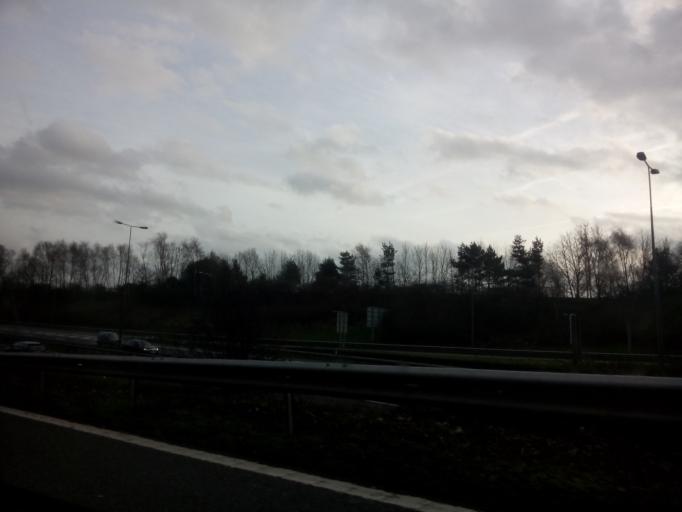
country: GB
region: England
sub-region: Worcestershire
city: Bromsgrove
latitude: 52.3545
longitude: -2.0446
